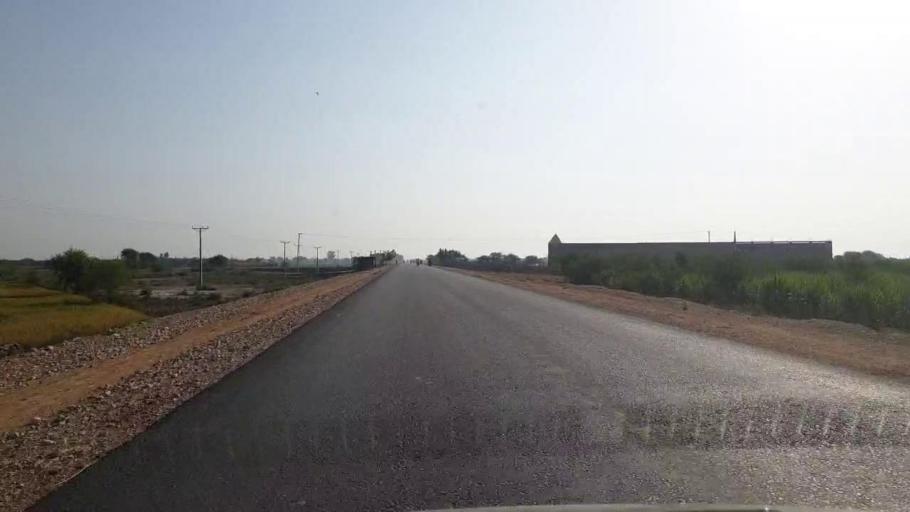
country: PK
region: Sindh
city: Badin
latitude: 24.6600
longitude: 68.8878
